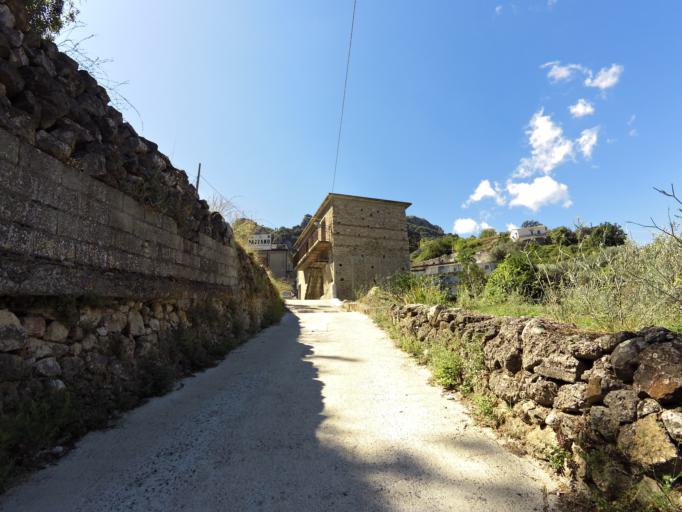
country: IT
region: Calabria
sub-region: Provincia di Reggio Calabria
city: Pazzano
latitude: 38.4783
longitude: 16.4512
